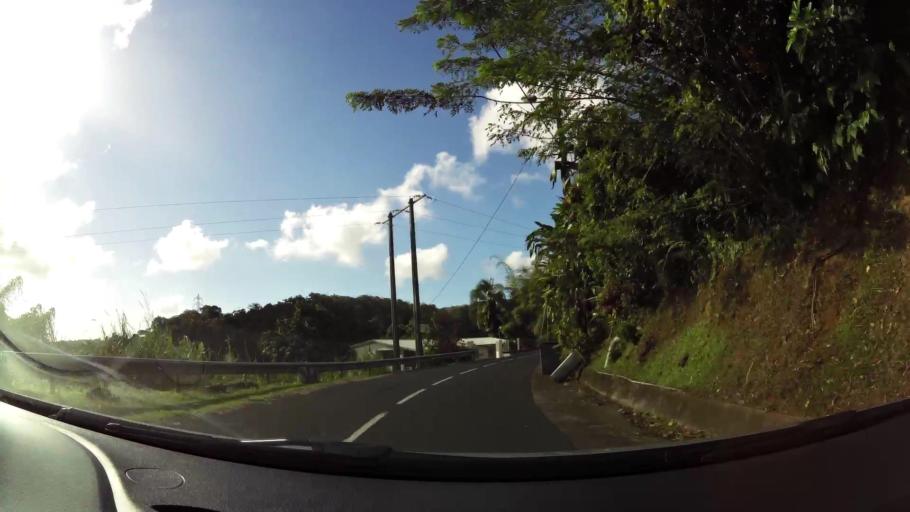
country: MQ
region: Martinique
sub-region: Martinique
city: Saint-Joseph
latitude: 14.6590
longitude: -61.0850
